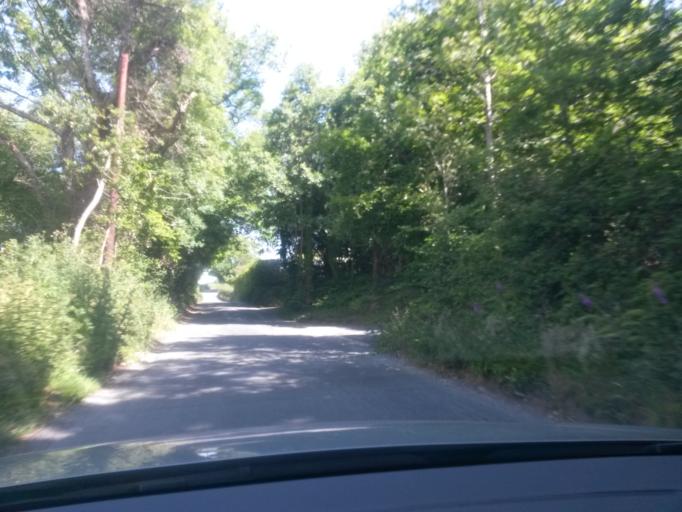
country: IE
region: Leinster
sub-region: Wicklow
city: Enniskerry
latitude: 53.1603
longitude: -6.1937
